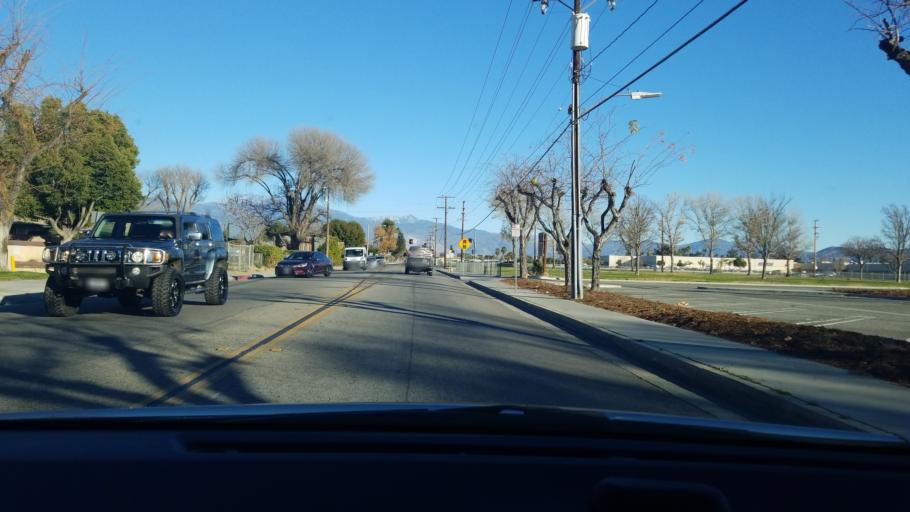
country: US
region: California
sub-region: Riverside County
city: Hemet
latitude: 33.7510
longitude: -116.9998
